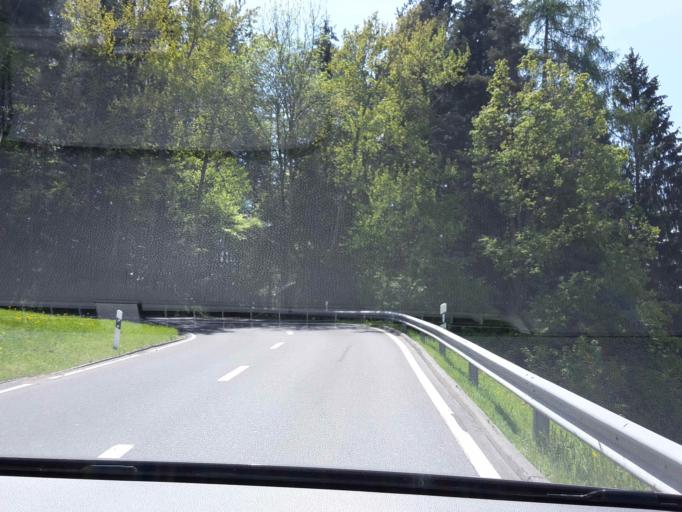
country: CH
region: Bern
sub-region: Thun District
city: Hilterfingen
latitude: 46.7517
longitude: 7.6588
